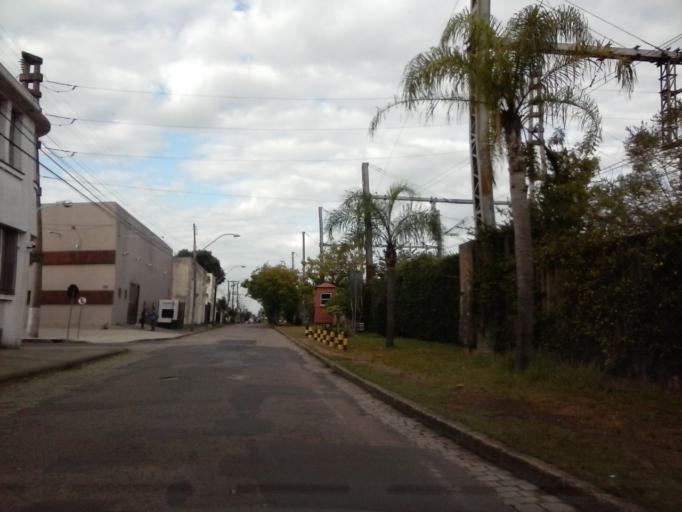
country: BR
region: Rio Grande do Sul
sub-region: Porto Alegre
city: Porto Alegre
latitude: -29.9972
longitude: -51.2015
